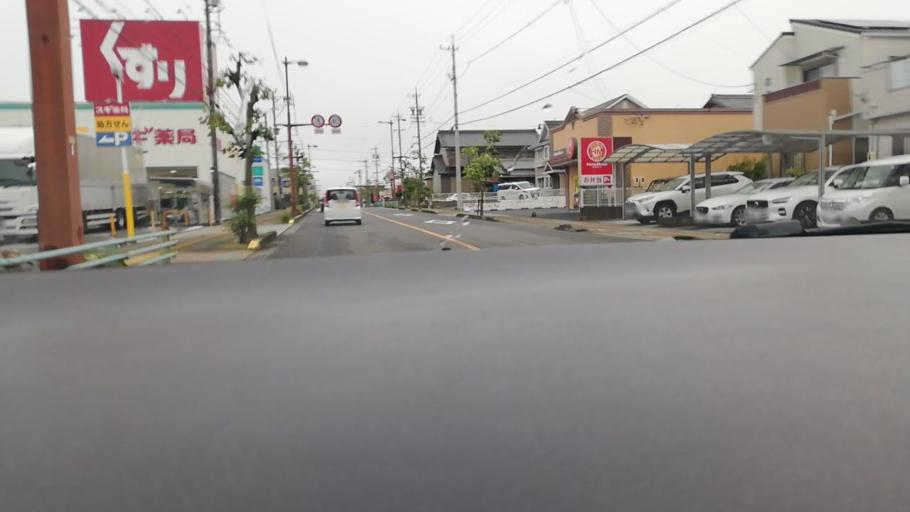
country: JP
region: Aichi
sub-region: Toyota-shi
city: Toyota
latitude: 35.0905
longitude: 137.1832
